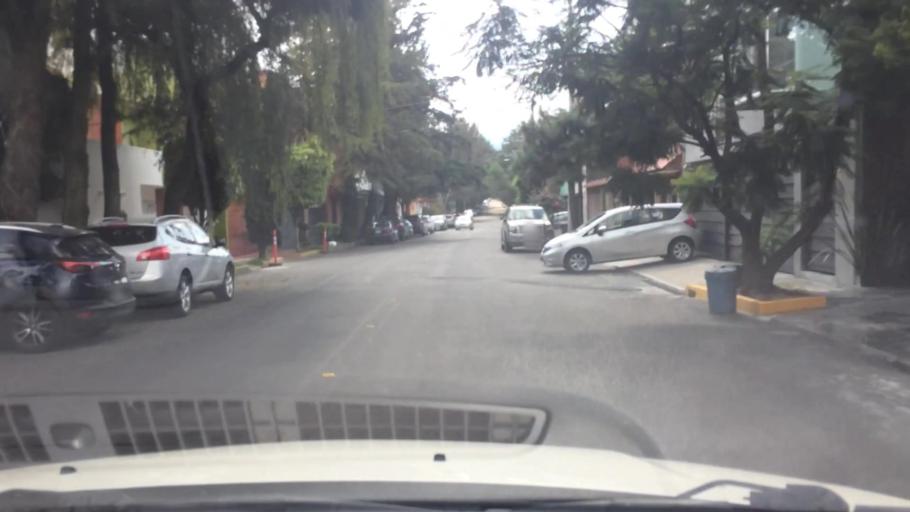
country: MX
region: Mexico City
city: Magdalena Contreras
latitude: 19.3416
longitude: -99.2437
